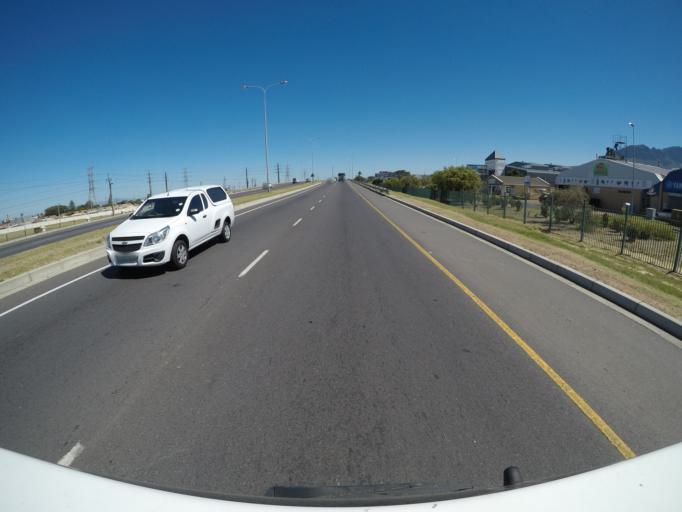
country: ZA
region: Western Cape
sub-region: Cape Winelands District Municipality
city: Stellenbosch
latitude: -34.1018
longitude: 18.8528
